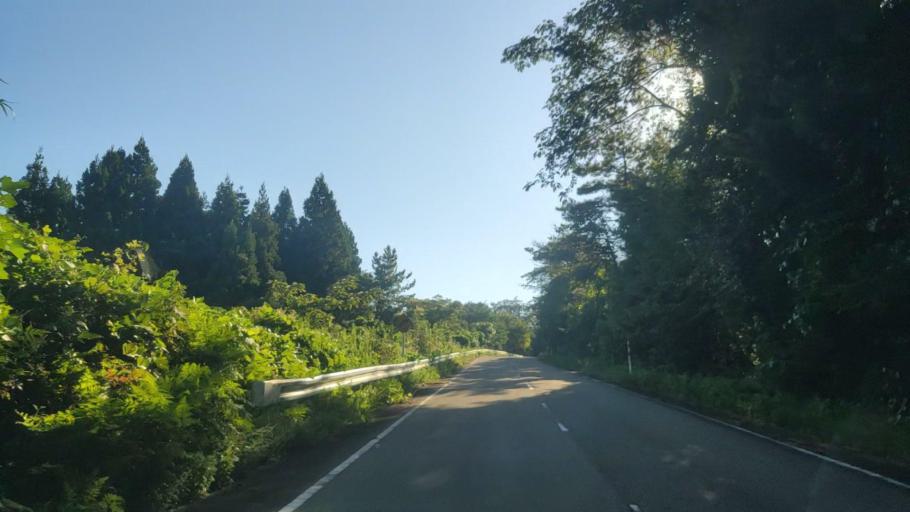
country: JP
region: Ishikawa
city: Nanao
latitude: 37.1166
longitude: 136.9539
